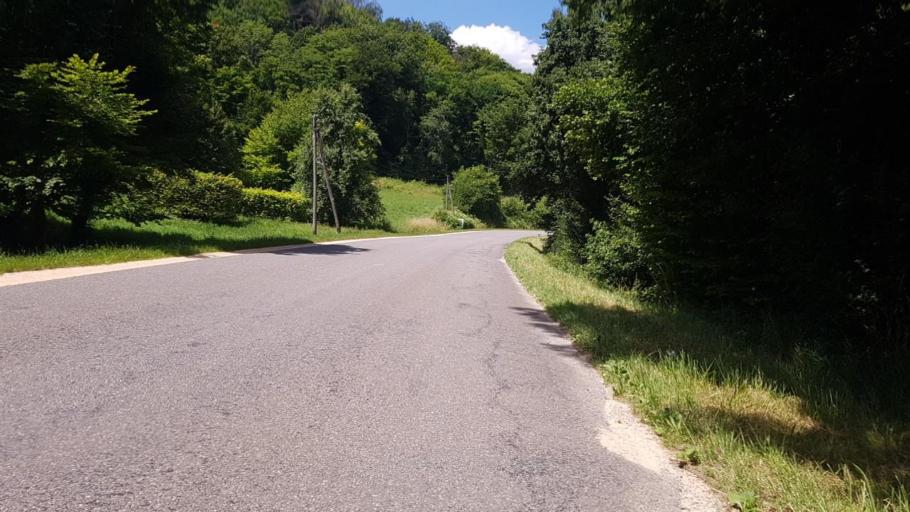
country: FR
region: Lorraine
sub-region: Departement de la Meuse
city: Gondrecourt-le-Chateau
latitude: 48.6332
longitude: 5.4538
